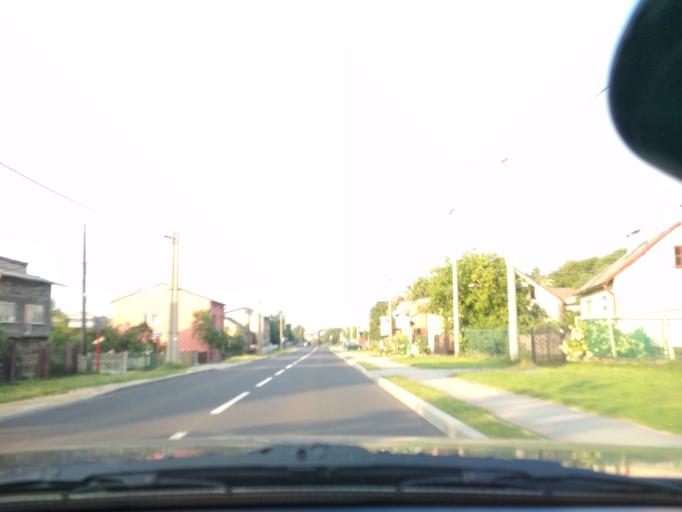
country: PL
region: Silesian Voivodeship
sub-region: Powiat zawiercianski
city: Ogrodzieniec
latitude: 50.4569
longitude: 19.5527
